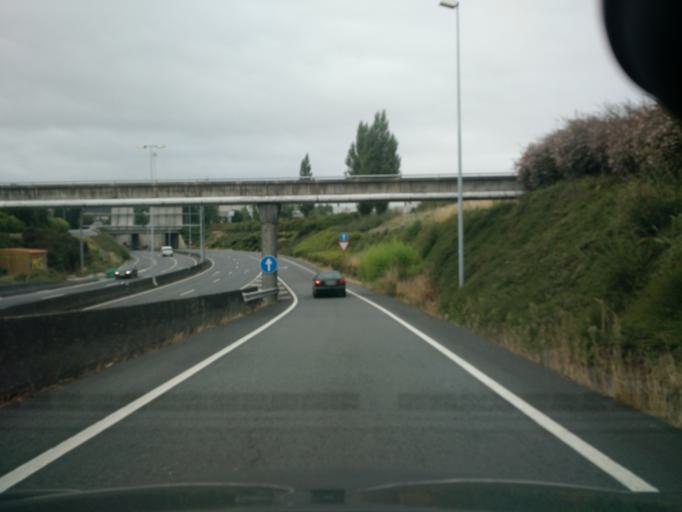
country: ES
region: Galicia
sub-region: Provincia da Coruna
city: Santiago de Compostela
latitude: 42.8888
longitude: -8.5101
